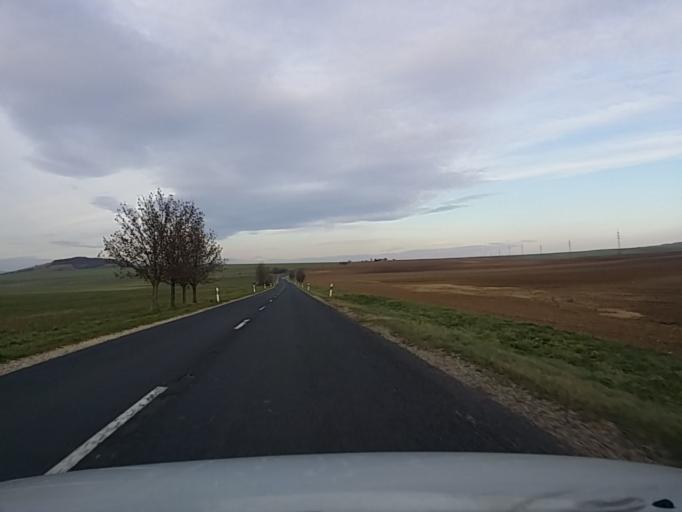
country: HU
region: Veszprem
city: Nemesvamos
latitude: 47.0357
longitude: 17.8169
